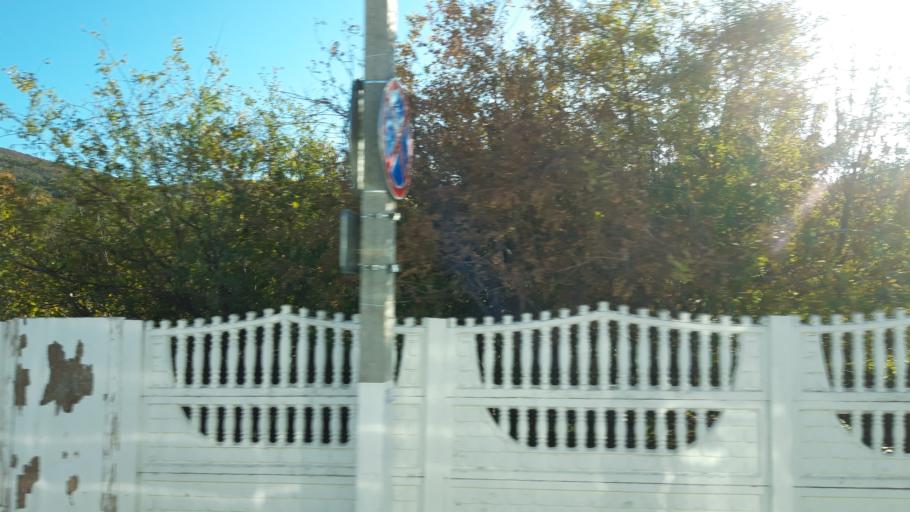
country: RU
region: Krasnodarskiy
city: Kabardinka
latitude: 44.6476
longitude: 37.9376
